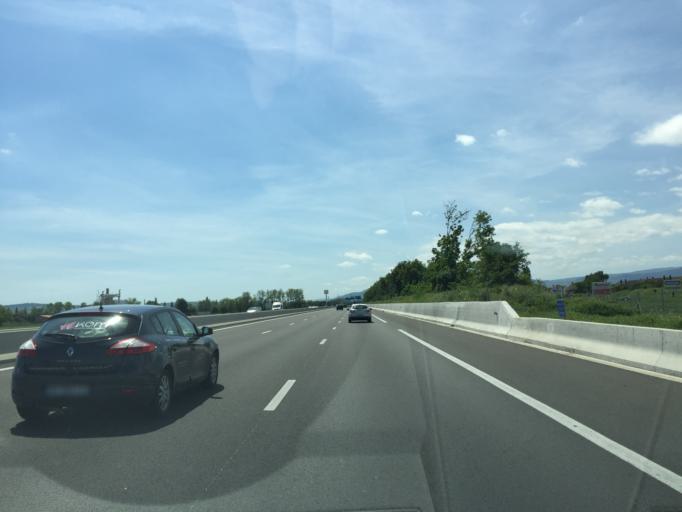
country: FR
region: Auvergne
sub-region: Departement du Puy-de-Dome
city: Gerzat
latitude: 45.8253
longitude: 3.1577
